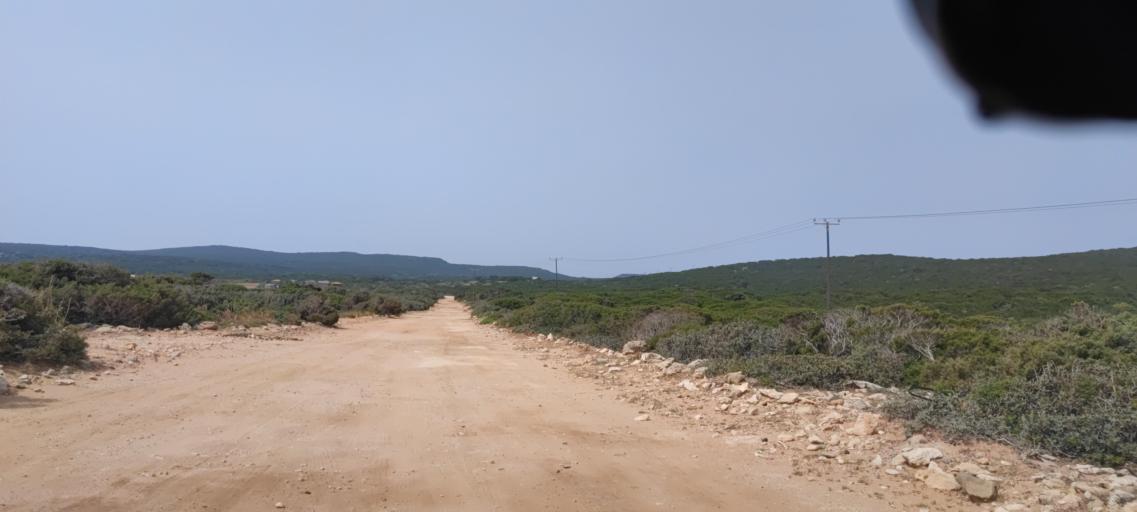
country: CY
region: Ammochostos
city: Rizokarpaso
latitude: 35.6725
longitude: 34.5760
